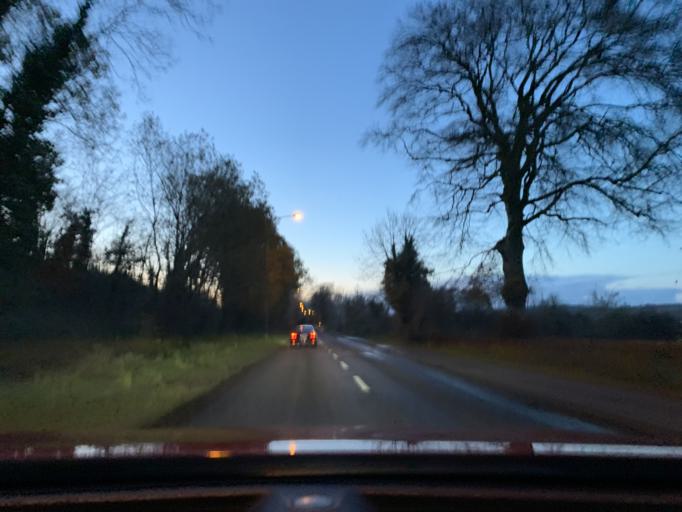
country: IE
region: Connaught
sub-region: Roscommon
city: Boyle
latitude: 53.9689
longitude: -8.2739
